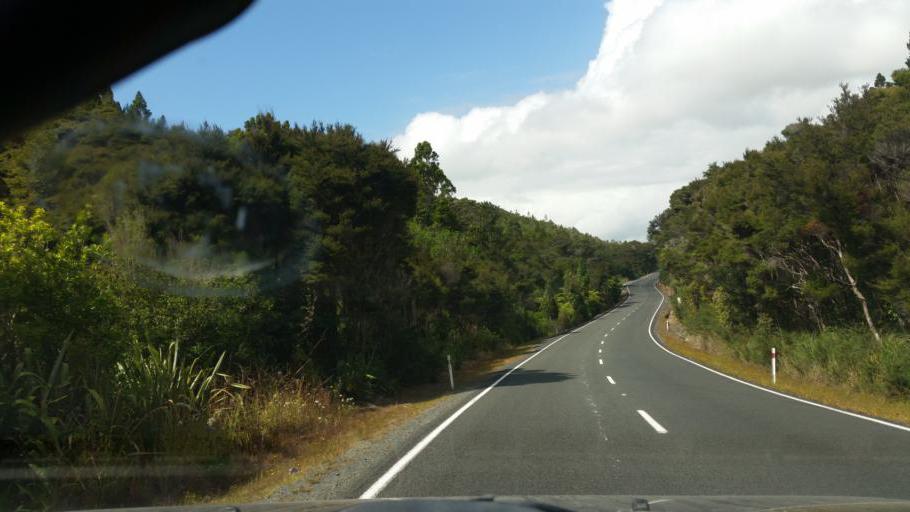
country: NZ
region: Northland
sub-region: Whangarei
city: Ruakaka
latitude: -36.0674
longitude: 174.5754
